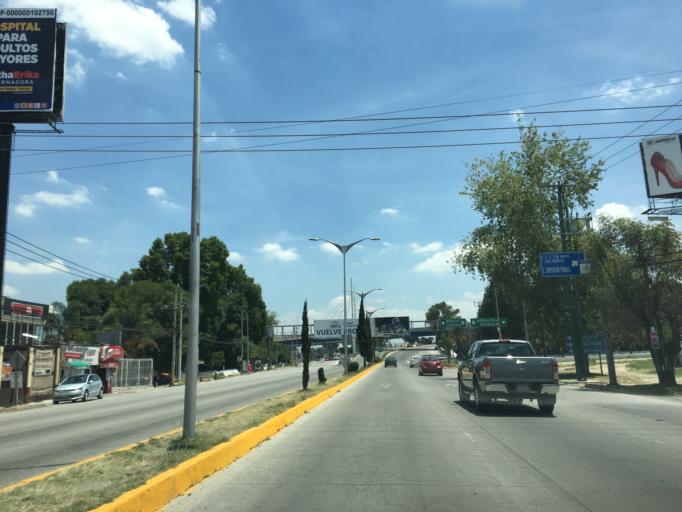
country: MX
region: Puebla
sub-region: Cuautlancingo
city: Sanctorum
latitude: 19.0943
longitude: -98.2299
